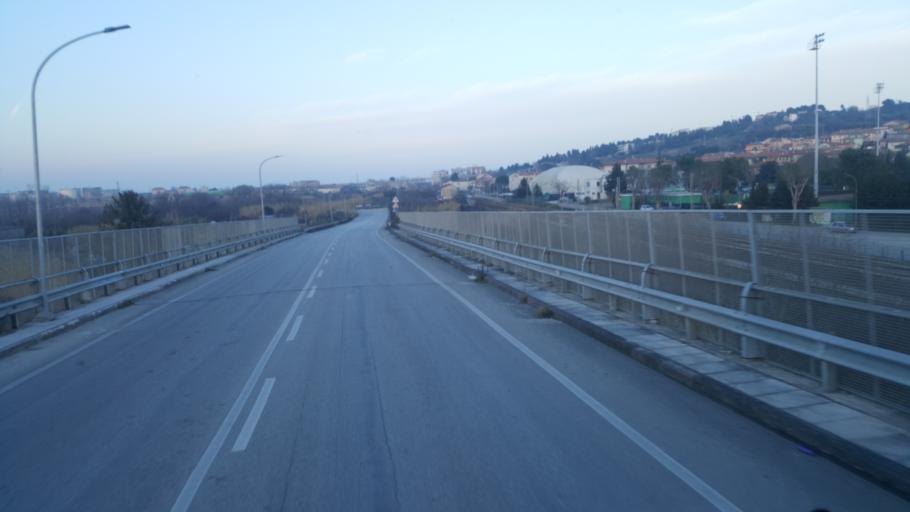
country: IT
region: The Marches
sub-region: Provincia di Ancona
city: Falconara Marittima
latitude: 43.6242
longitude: 13.3782
